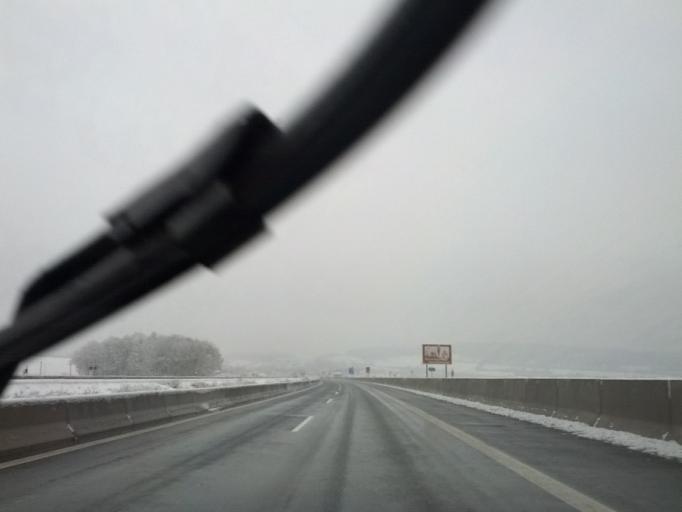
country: DE
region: Bavaria
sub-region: Regierungsbezirk Unterfranken
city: Munnerstadt
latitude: 50.2343
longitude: 10.2201
